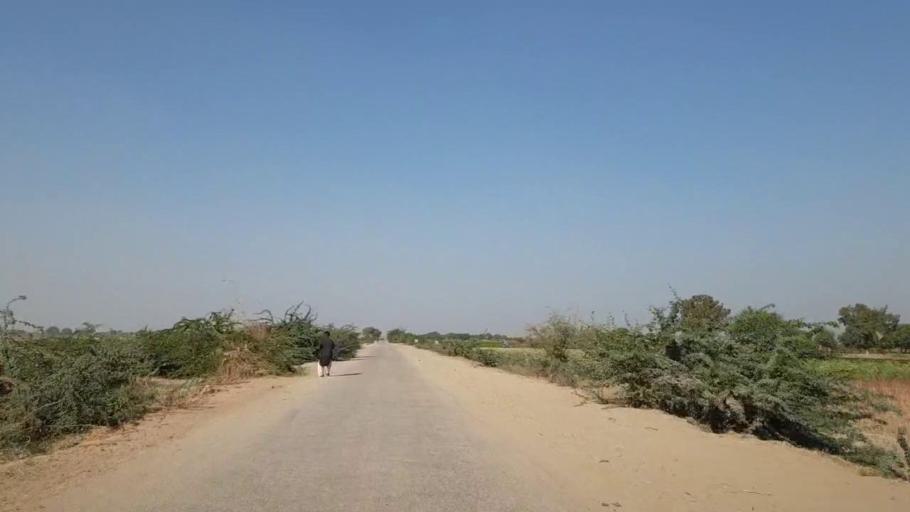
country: PK
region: Sindh
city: Digri
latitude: 25.0145
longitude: 69.1060
